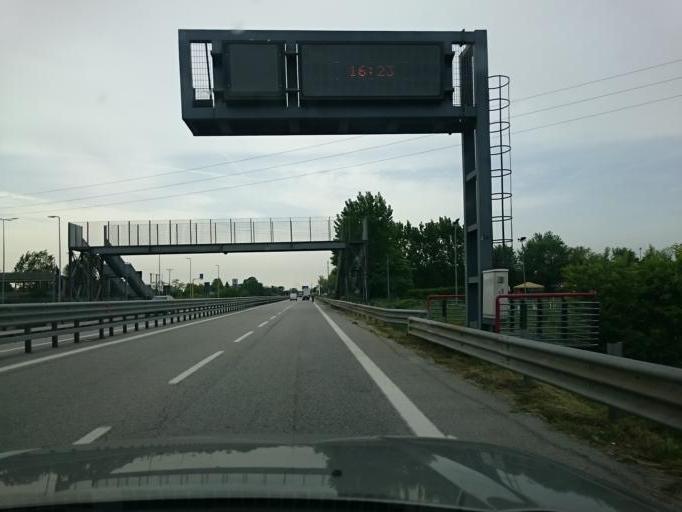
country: IT
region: Veneto
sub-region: Provincia di Venezia
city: Campalto
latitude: 45.5075
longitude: 12.2688
